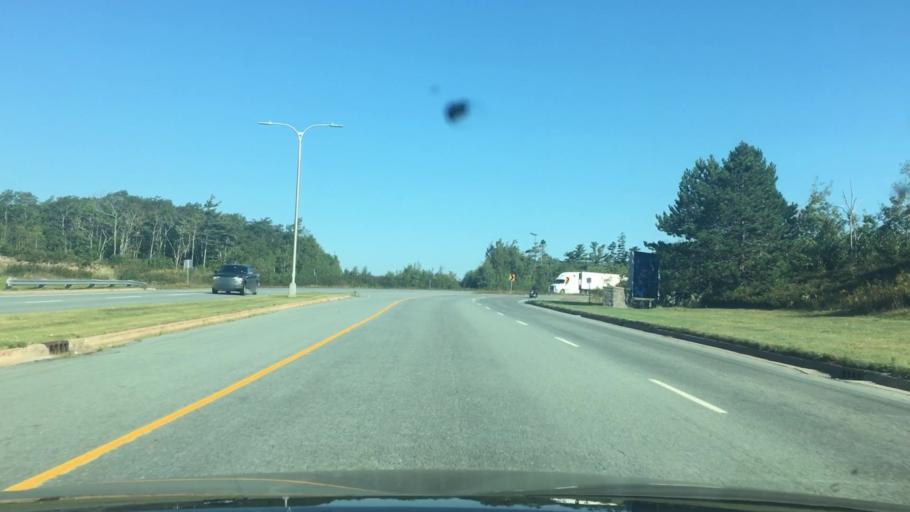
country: CA
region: Nova Scotia
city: Dartmouth
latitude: 44.7202
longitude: -63.5806
